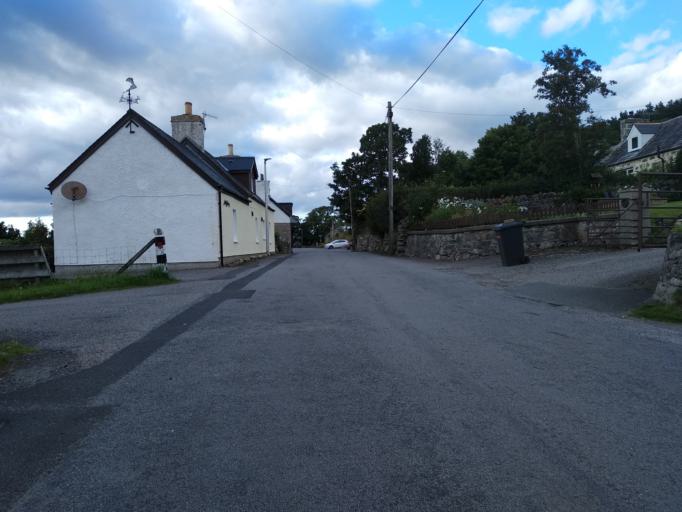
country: GB
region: Scotland
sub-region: Highland
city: Golspie
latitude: 58.4748
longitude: -4.4168
